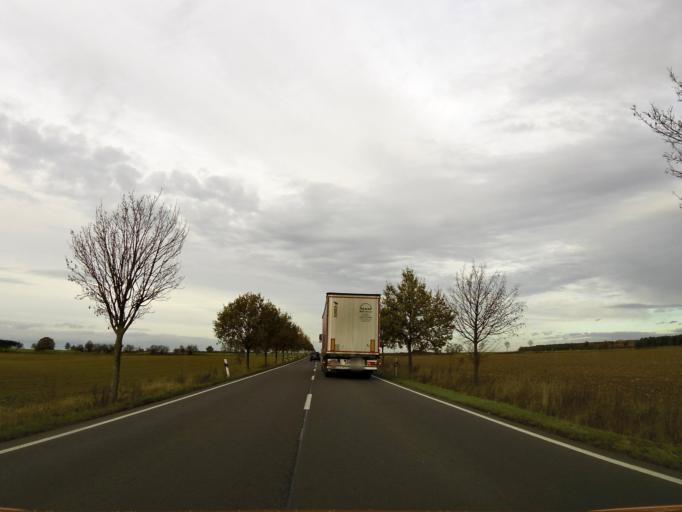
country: DE
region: Saxony-Anhalt
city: Pretzier
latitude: 52.7168
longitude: 11.2496
